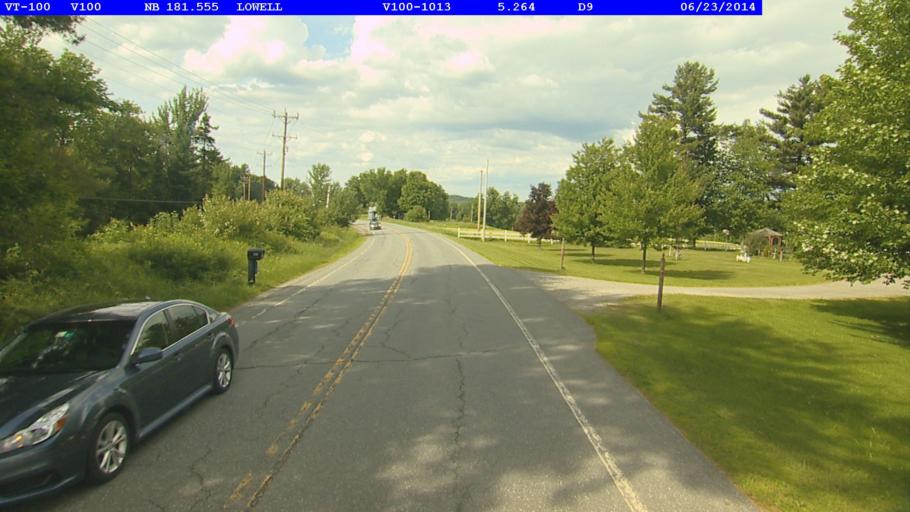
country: US
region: Vermont
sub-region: Orleans County
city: Newport
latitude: 44.8115
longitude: -72.4445
